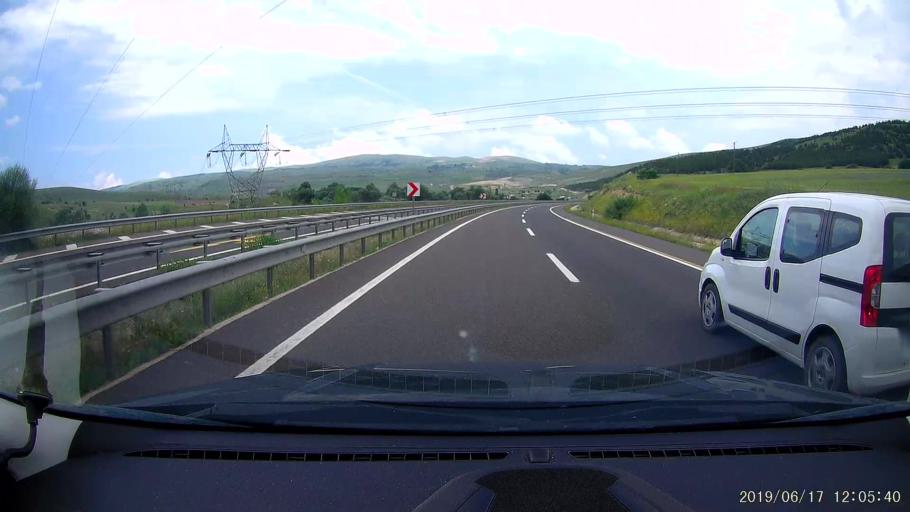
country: TR
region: Cankiri
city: Cerkes
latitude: 40.8339
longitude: 32.7735
